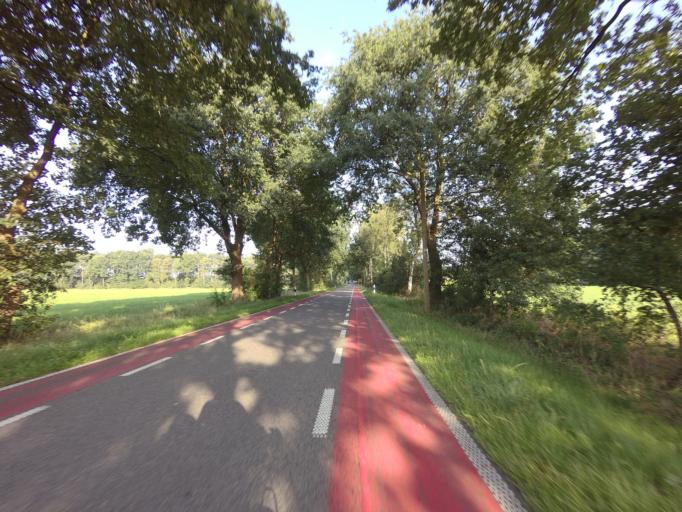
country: DE
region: Lower Saxony
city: Getelo
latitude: 52.4652
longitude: 6.8459
